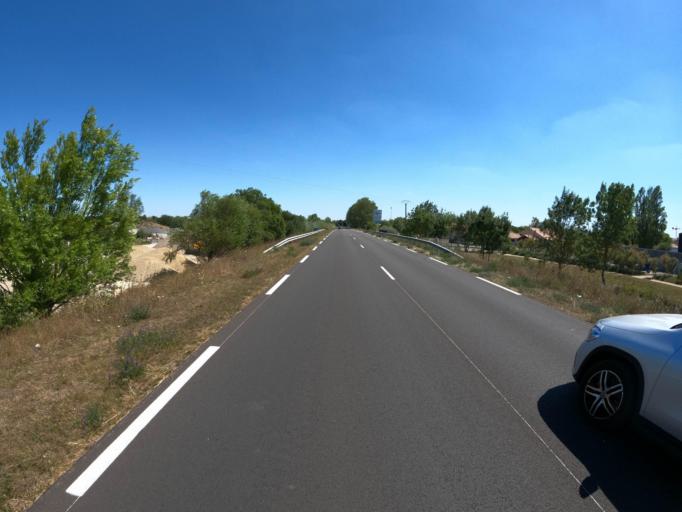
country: FR
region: Pays de la Loire
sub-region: Departement de la Vendee
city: Saint-Jean-de-Monts
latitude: 46.8000
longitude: -2.0609
